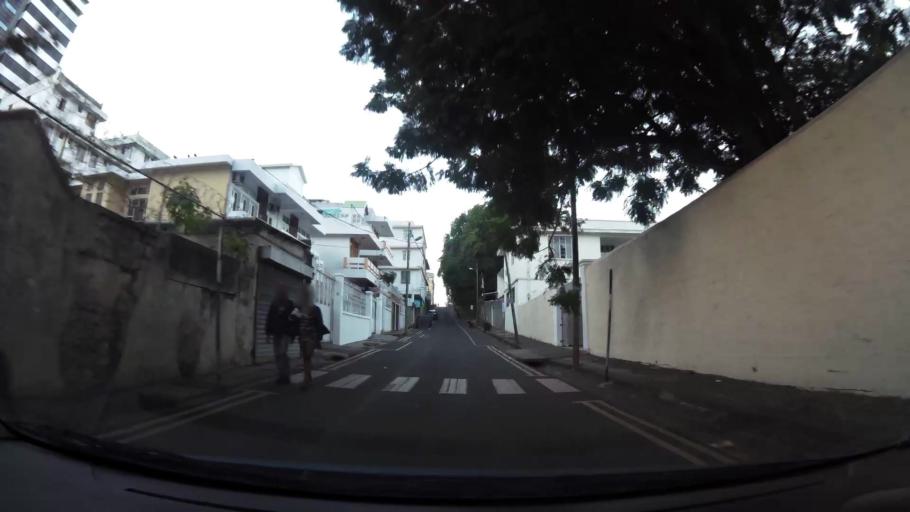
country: MU
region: Port Louis
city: Port Louis
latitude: -20.1635
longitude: 57.5071
